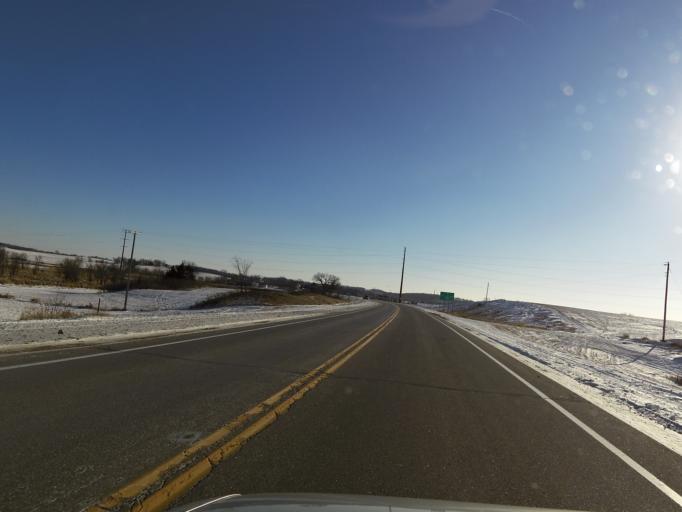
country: US
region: Minnesota
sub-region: Le Sueur County
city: New Prague
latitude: 44.5768
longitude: -93.5064
